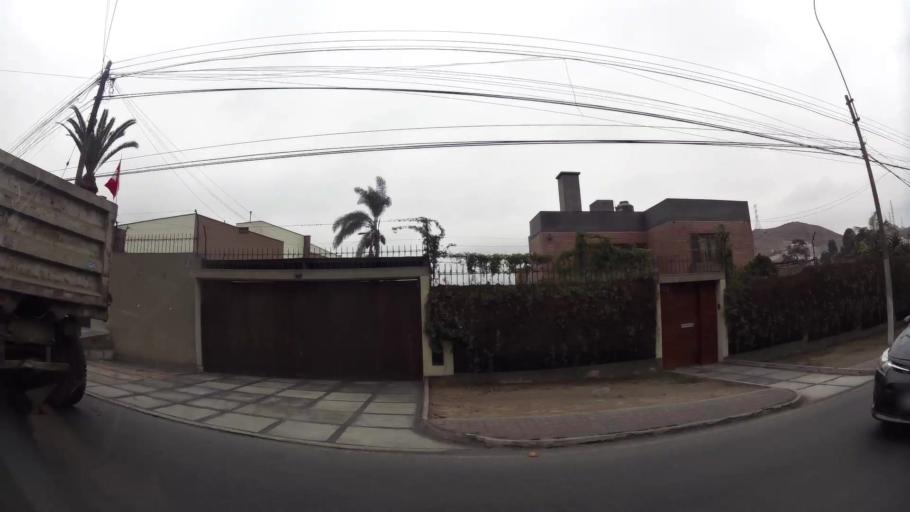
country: PE
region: Lima
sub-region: Lima
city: La Molina
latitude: -12.0748
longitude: -76.9574
